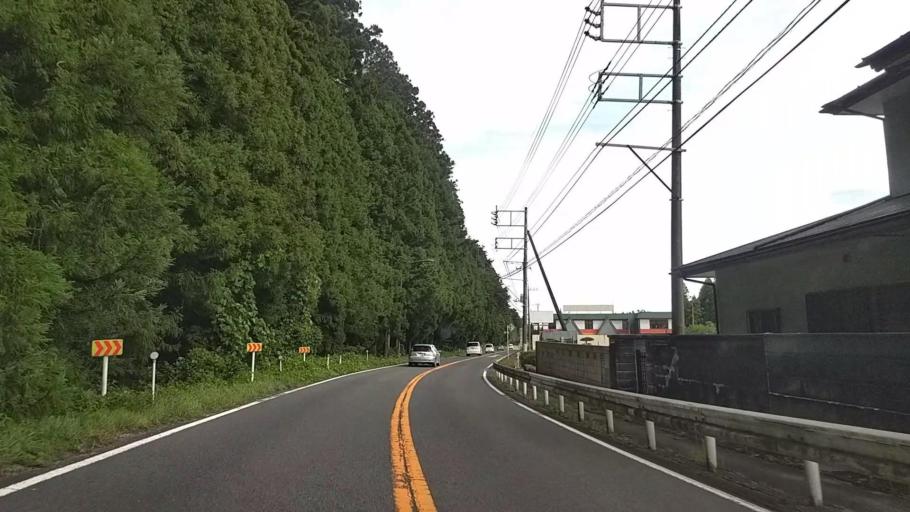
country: JP
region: Tochigi
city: Imaichi
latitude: 36.7327
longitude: 139.6608
